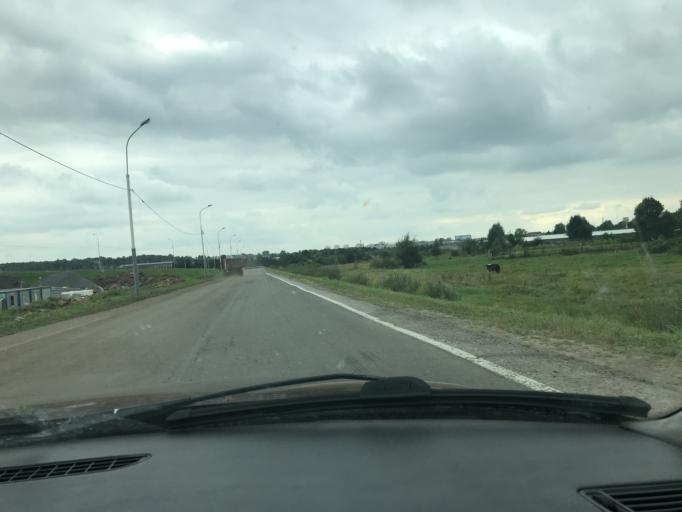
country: RU
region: Kaluga
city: Kaluga
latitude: 54.5564
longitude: 36.3363
